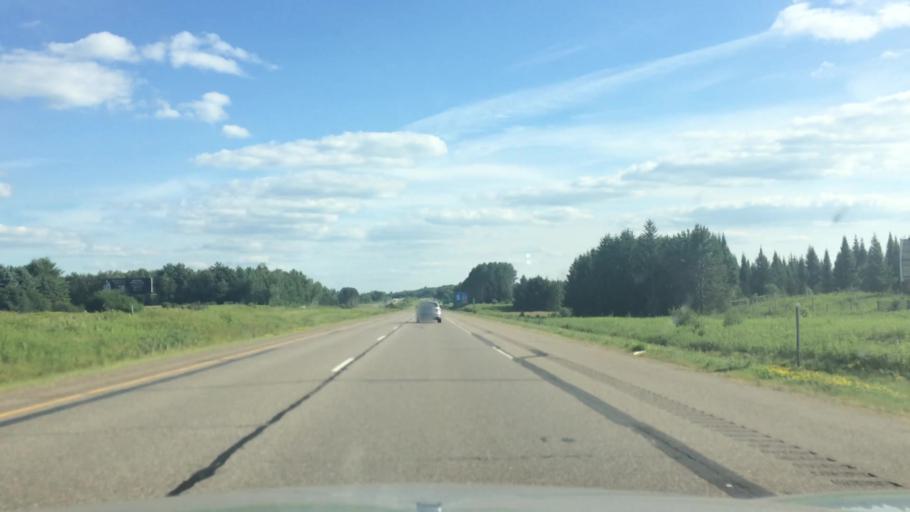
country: US
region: Wisconsin
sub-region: Lincoln County
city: Merrill
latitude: 45.1888
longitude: -89.6466
